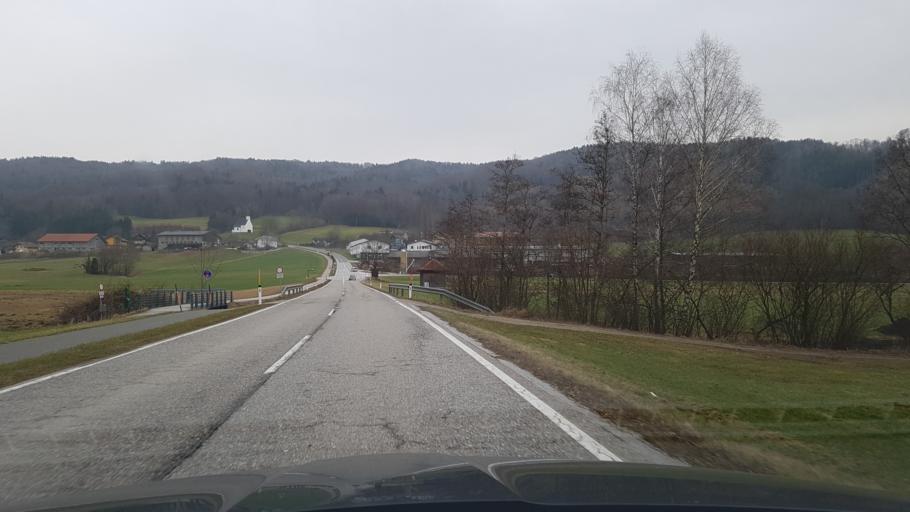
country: AT
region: Salzburg
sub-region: Politischer Bezirk Salzburg-Umgebung
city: Dorfbeuern
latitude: 48.0040
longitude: 13.0322
